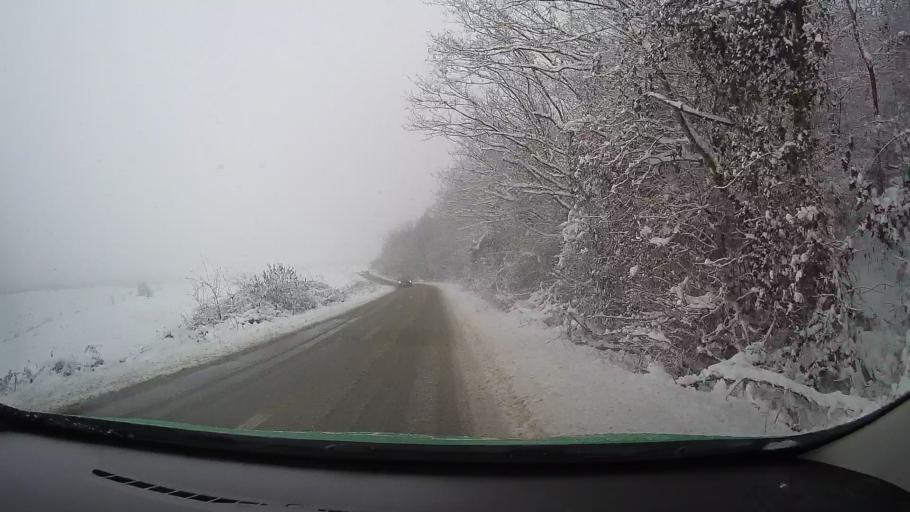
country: RO
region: Hunedoara
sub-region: Comuna Teliucu Inferior
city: Teliucu Inferior
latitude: 45.6892
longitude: 22.9077
